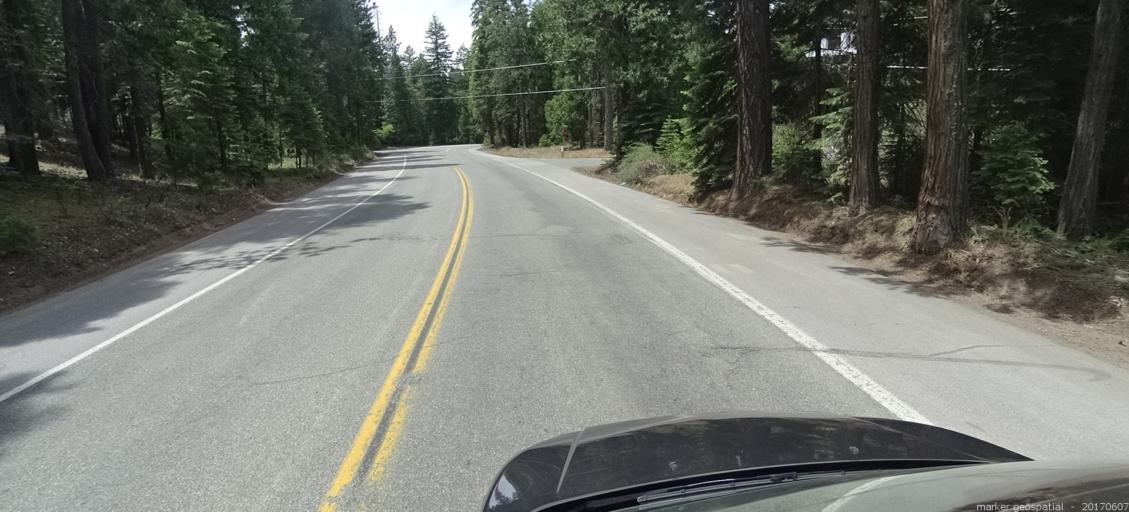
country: US
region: California
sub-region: Siskiyou County
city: Mount Shasta
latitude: 41.3319
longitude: -122.3470
